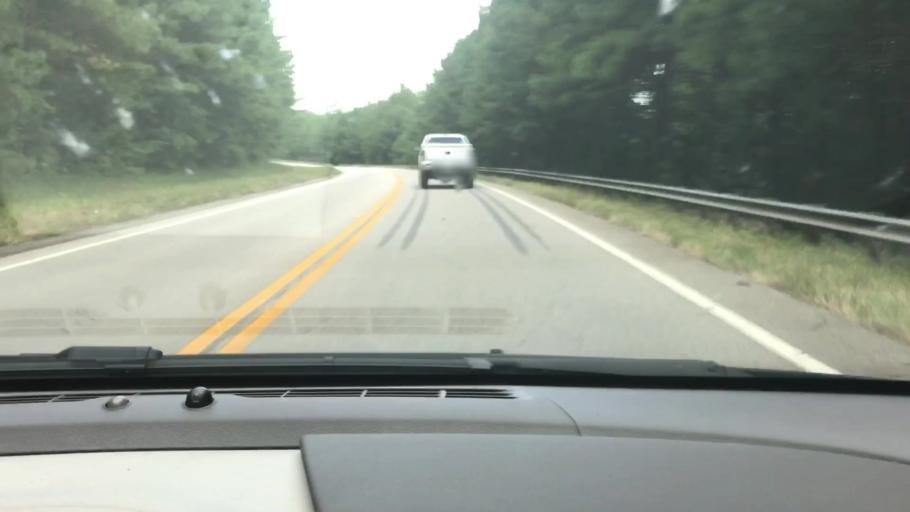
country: US
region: Georgia
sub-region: Troup County
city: La Grange
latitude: 32.9696
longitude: -85.0239
